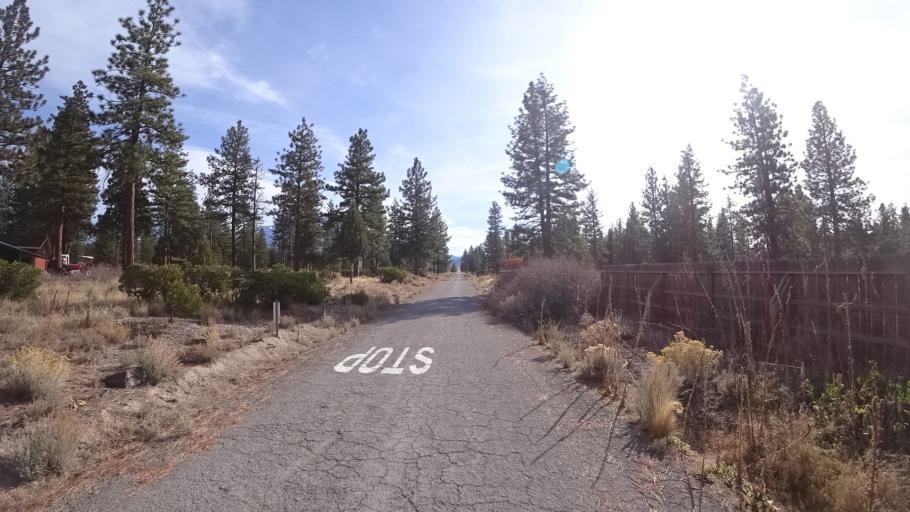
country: US
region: California
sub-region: Siskiyou County
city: Weed
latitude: 41.4929
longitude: -122.3739
